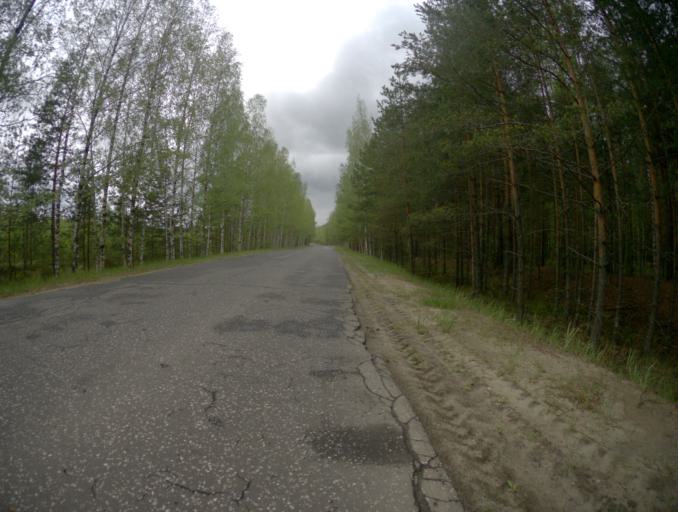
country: RU
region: Vladimir
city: Zolotkovo
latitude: 55.3517
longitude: 40.9233
